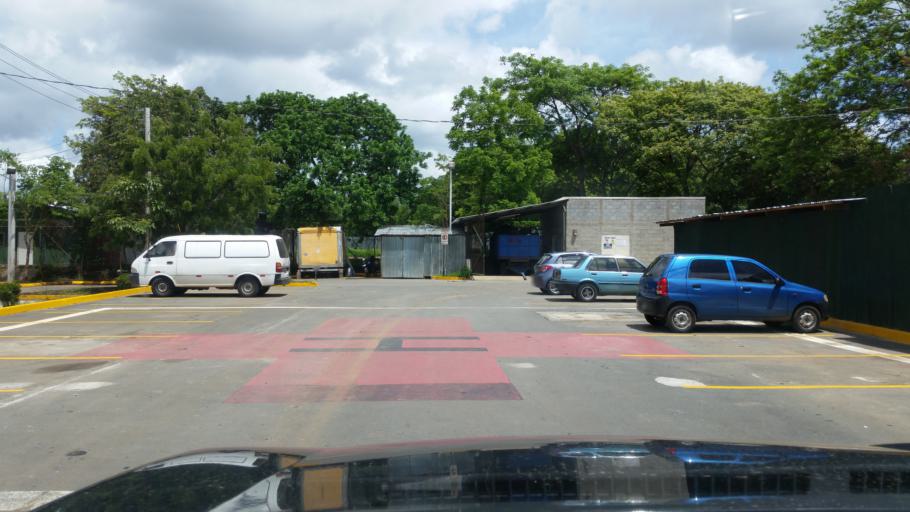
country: NI
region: Managua
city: Managua
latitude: 12.0860
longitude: -86.2351
